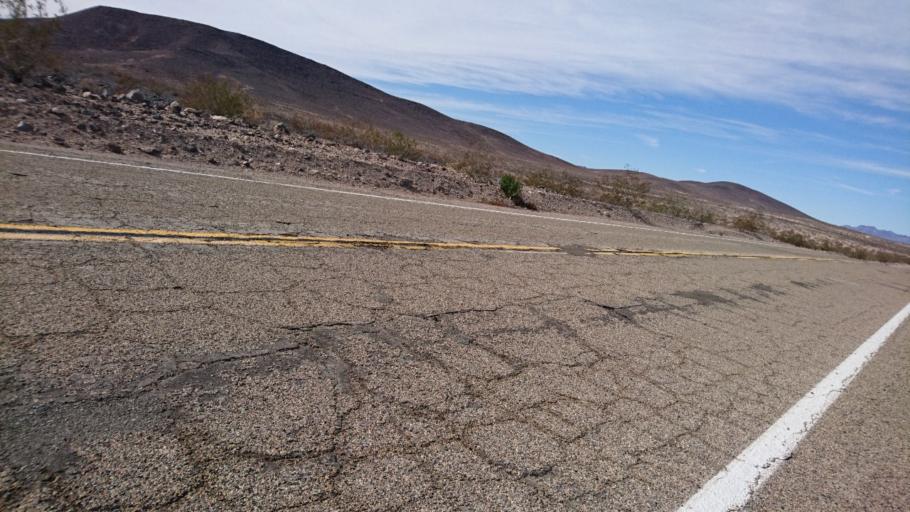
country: US
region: California
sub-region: San Bernardino County
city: Twentynine Palms
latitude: 34.6880
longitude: -116.0390
